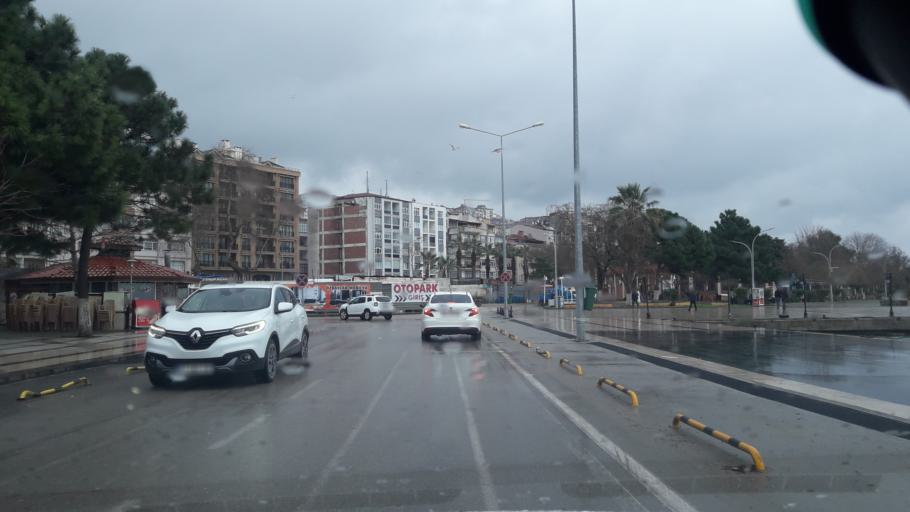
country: TR
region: Sinop
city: Sinop
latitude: 42.0237
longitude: 35.1513
